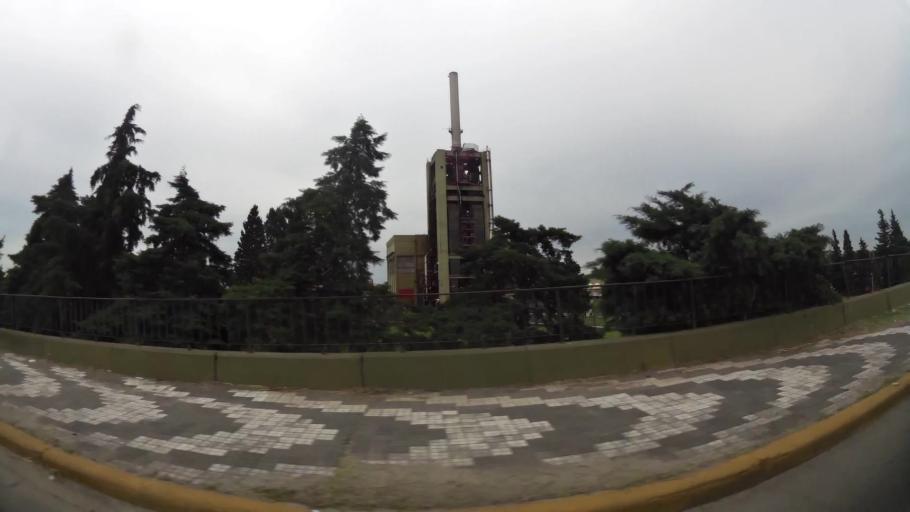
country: AR
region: Santa Fe
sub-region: Departamento de Rosario
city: Rosario
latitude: -32.9052
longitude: -60.6783
